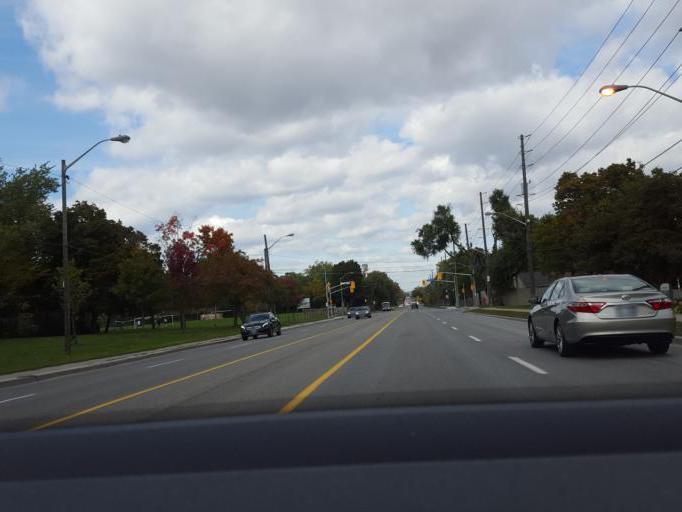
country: CA
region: Ontario
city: Willowdale
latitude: 43.7399
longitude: -79.3571
